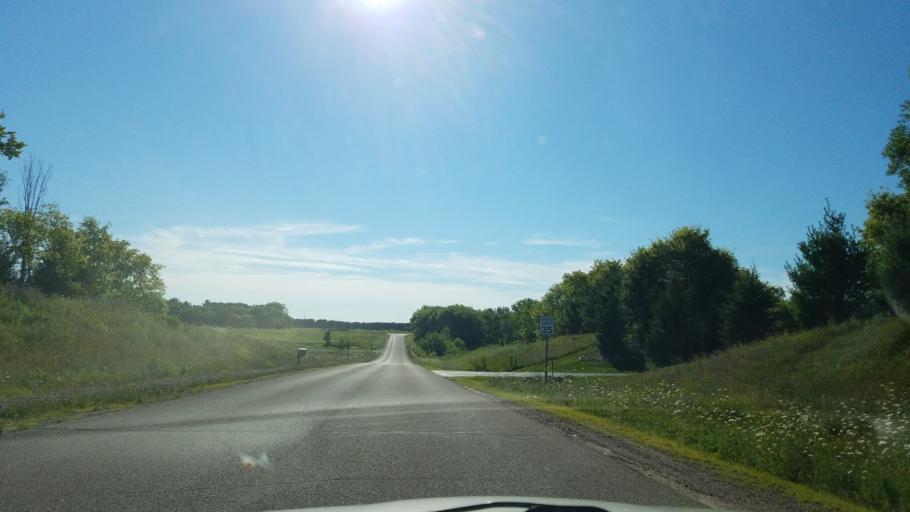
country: US
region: Wisconsin
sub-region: Saint Croix County
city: Somerset
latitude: 45.1109
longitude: -92.7216
